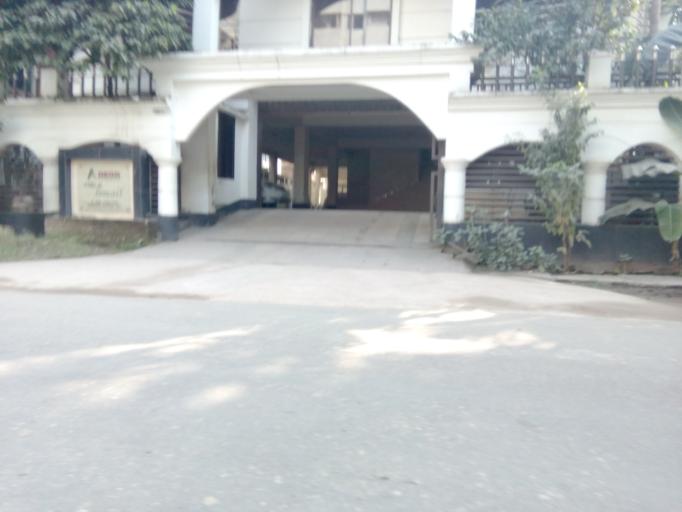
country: BD
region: Dhaka
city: Tungi
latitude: 23.8185
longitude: 90.4309
